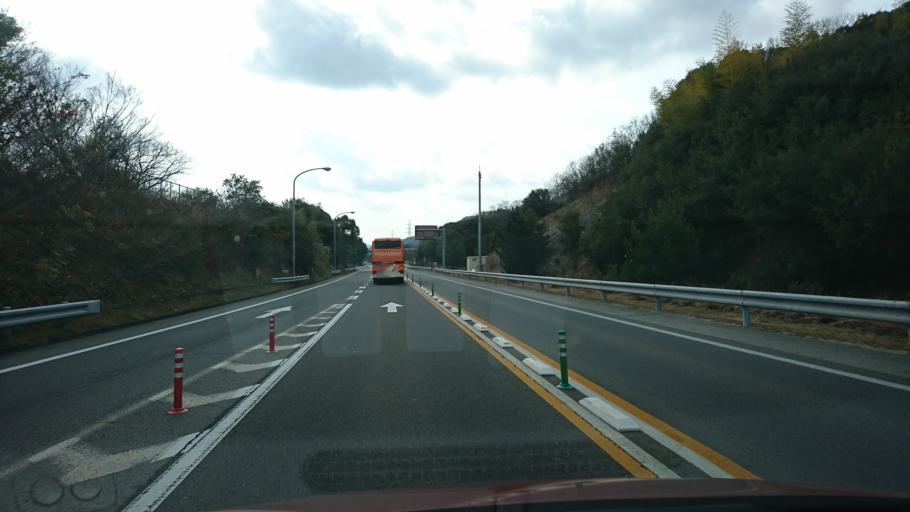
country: JP
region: Hiroshima
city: Innoshima
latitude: 34.2472
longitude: 133.0482
